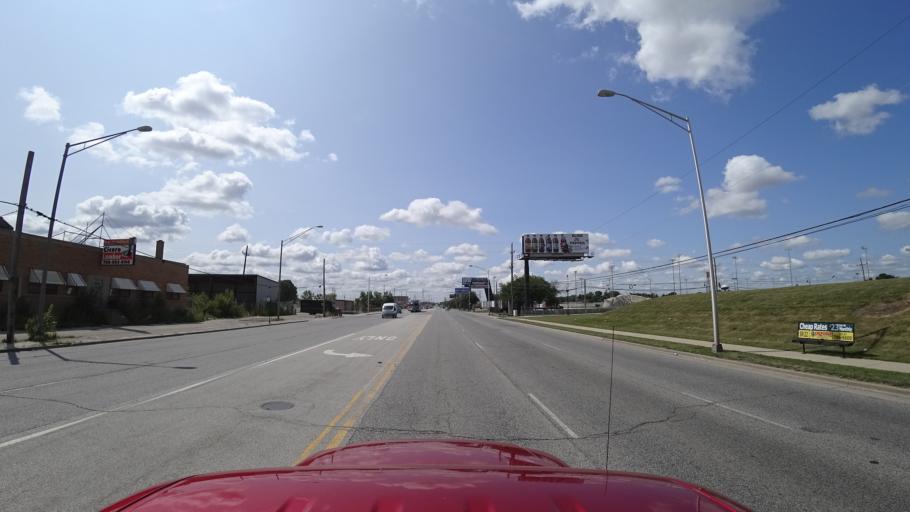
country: US
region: Illinois
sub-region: Cook County
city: Cicero
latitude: 41.8299
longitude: -87.7437
